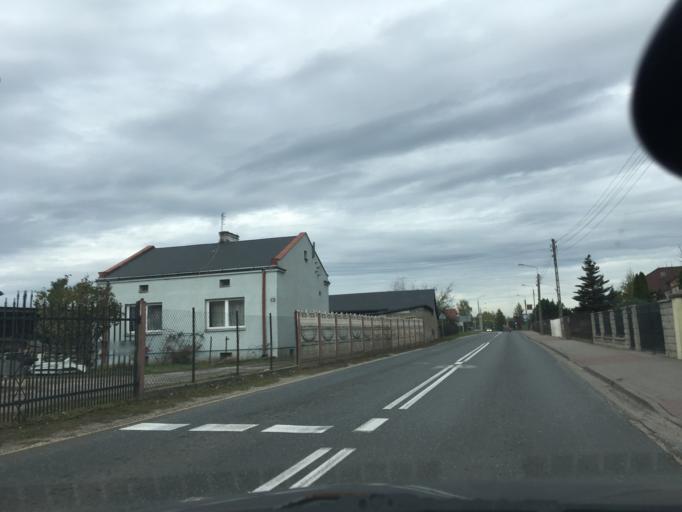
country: PL
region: Masovian Voivodeship
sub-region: Powiat zyrardowski
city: Mszczonow
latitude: 51.9739
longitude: 20.5296
